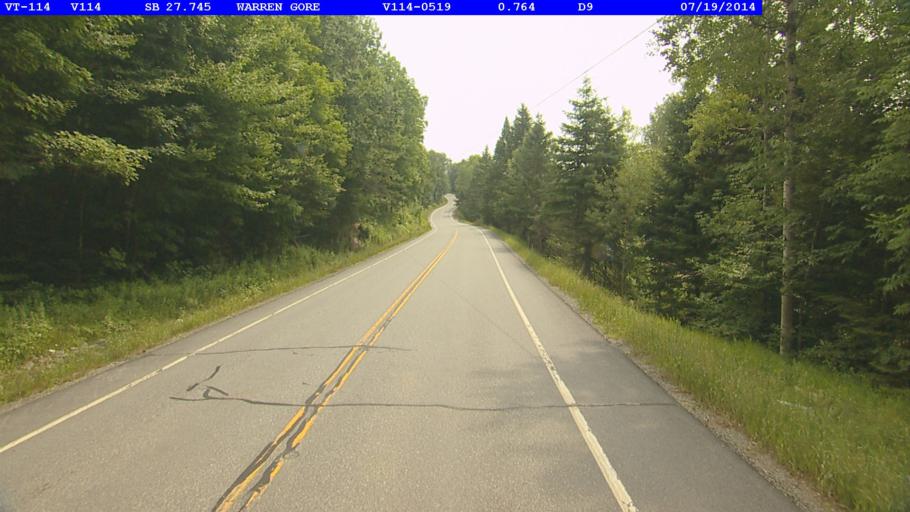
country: CA
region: Quebec
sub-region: Estrie
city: Coaticook
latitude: 44.8974
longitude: -71.8872
